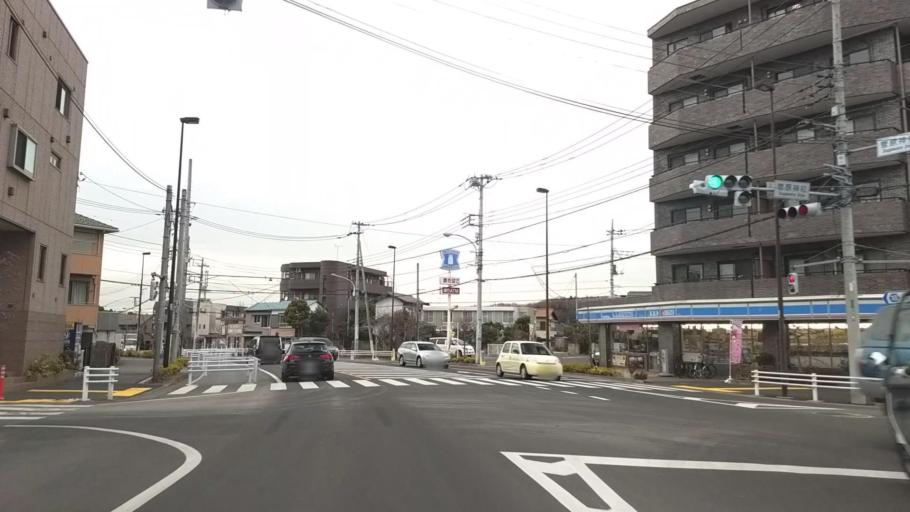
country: JP
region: Tokyo
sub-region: Machida-shi
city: Machida
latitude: 35.5603
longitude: 139.4482
